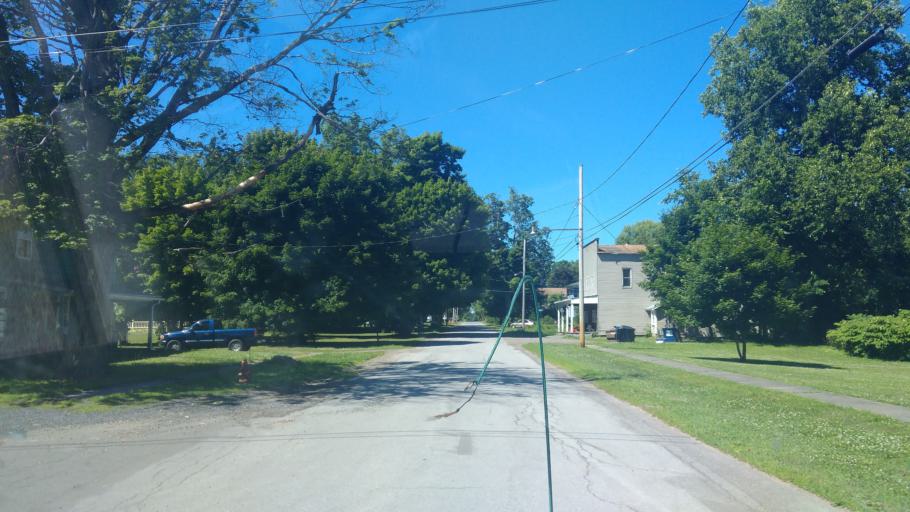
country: US
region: New York
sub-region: Wayne County
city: Sodus
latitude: 43.2020
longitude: -77.0252
